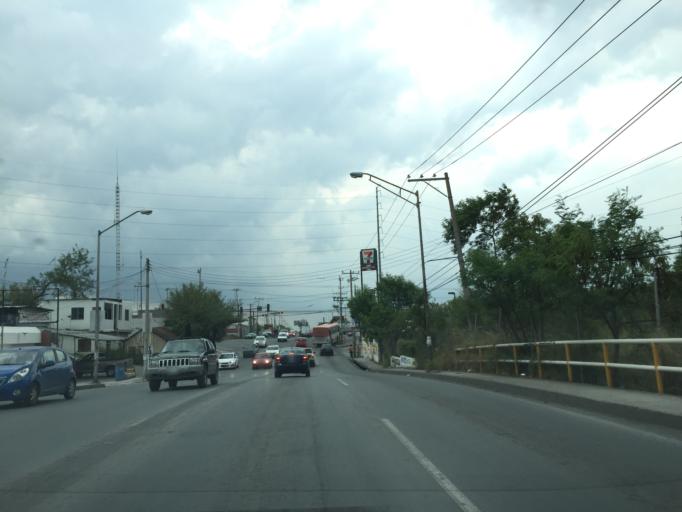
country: MX
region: Nuevo Leon
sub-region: Juarez
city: Valle de Juarez
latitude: 25.6660
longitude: -100.1743
